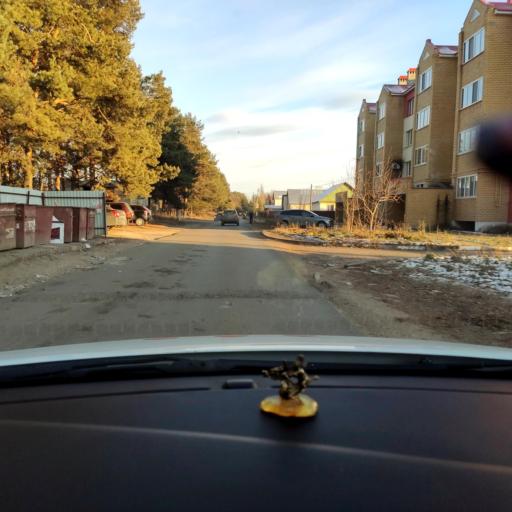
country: RU
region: Tatarstan
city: Stolbishchi
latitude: 55.6125
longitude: 49.1354
